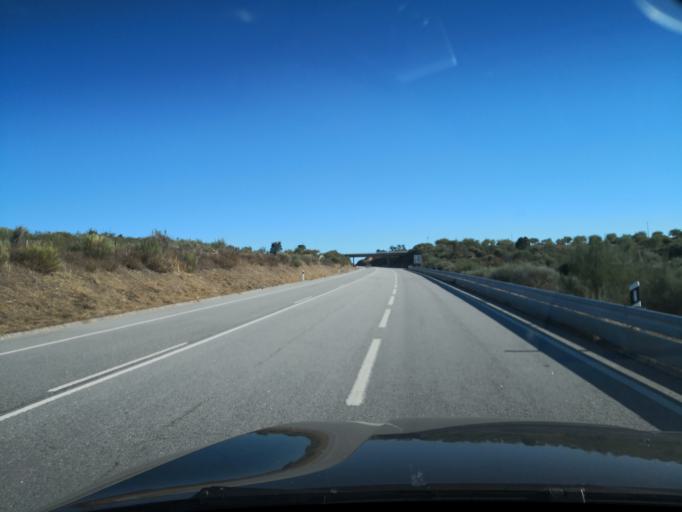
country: PT
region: Braganca
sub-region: Mirandela
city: Mirandela
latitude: 41.4942
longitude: -7.2277
